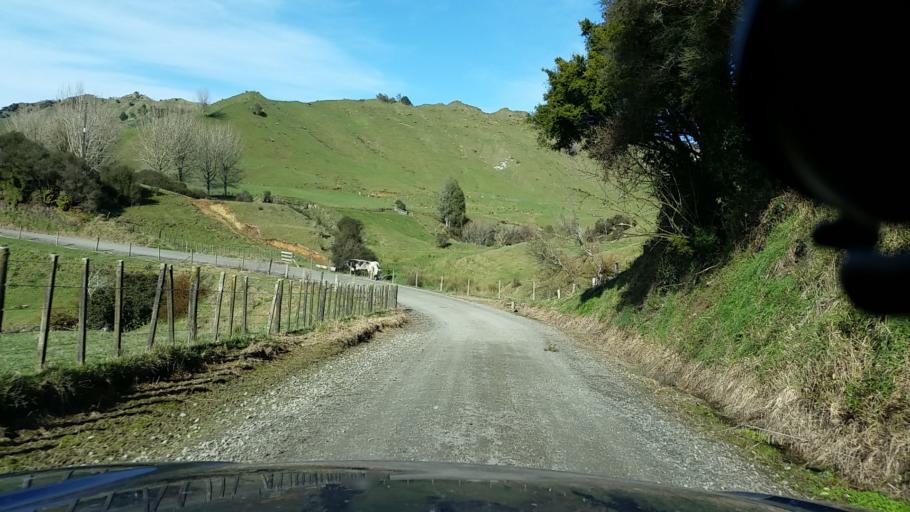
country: NZ
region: Taranaki
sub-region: New Plymouth District
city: Waitara
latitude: -39.0568
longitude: 174.7741
